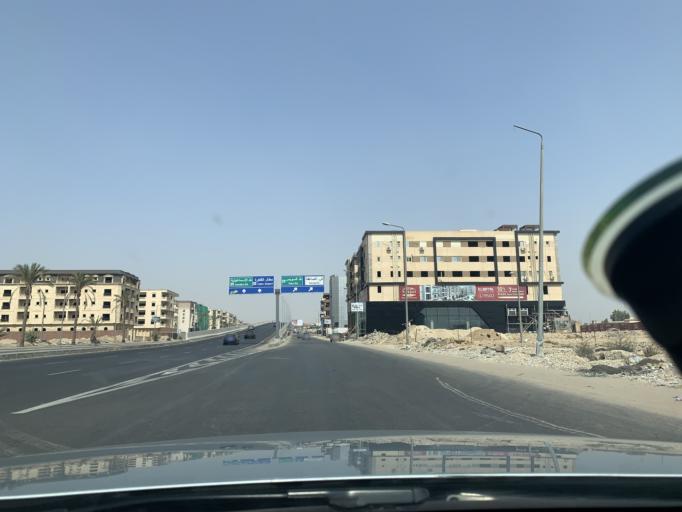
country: EG
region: Muhafazat al Qalyubiyah
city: Al Khankah
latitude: 30.0910
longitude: 31.3723
